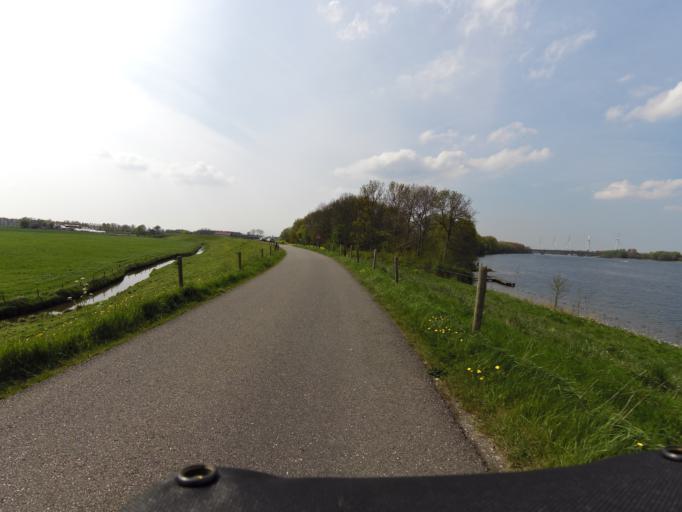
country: NL
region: South Holland
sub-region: Gemeente Maassluis
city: Maassluis
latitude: 51.8898
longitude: 4.2176
